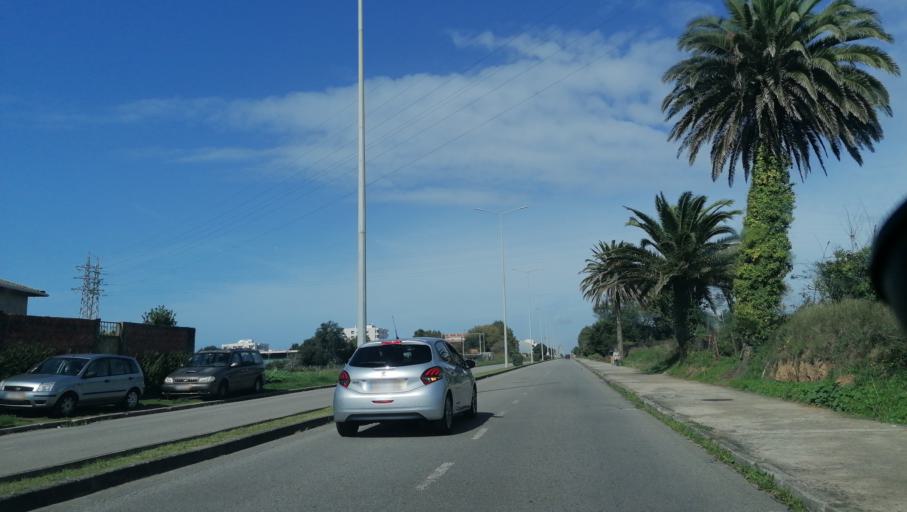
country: PT
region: Aveiro
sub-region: Espinho
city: Silvalde
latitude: 40.9998
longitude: -8.6343
